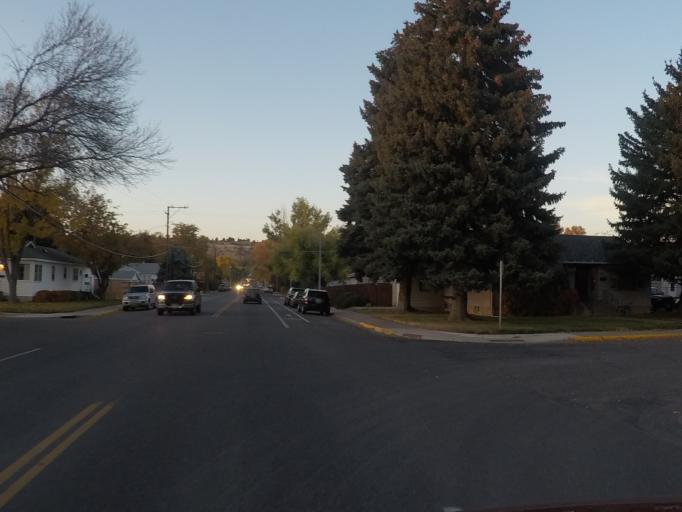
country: US
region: Montana
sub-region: Yellowstone County
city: Billings
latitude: 45.7878
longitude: -108.5486
